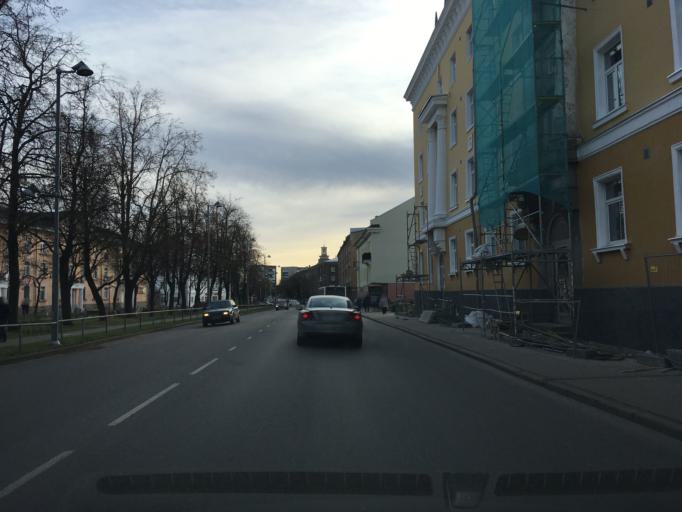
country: EE
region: Ida-Virumaa
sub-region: Narva linn
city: Narva
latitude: 59.3753
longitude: 28.1939
